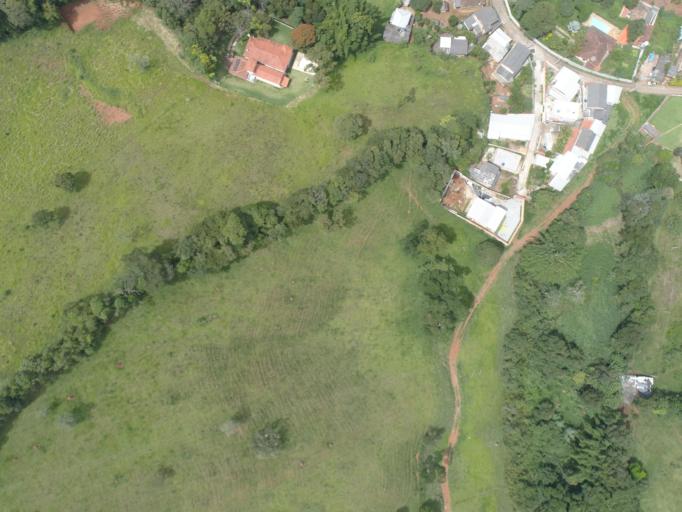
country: BR
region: Minas Gerais
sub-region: Tiradentes
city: Tiradentes
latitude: -21.0672
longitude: -44.0844
